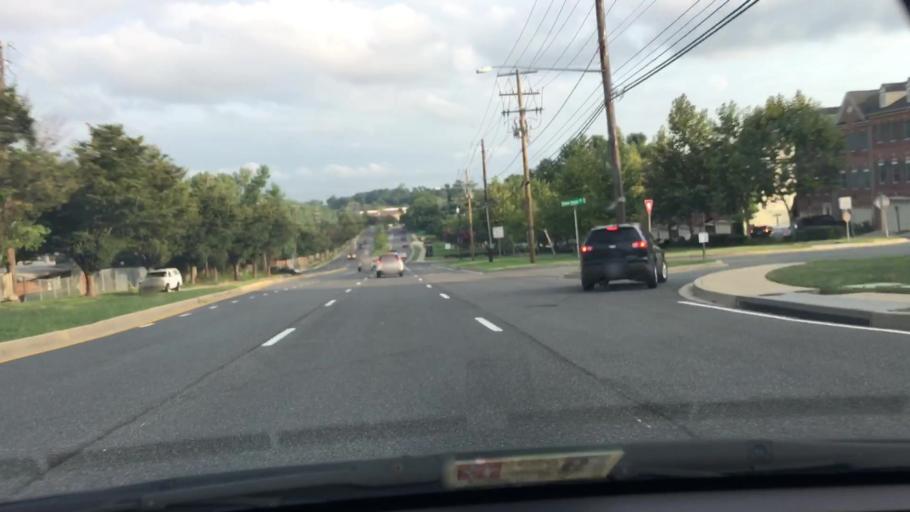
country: US
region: Maryland
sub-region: Montgomery County
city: Germantown
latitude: 39.1869
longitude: -77.2403
